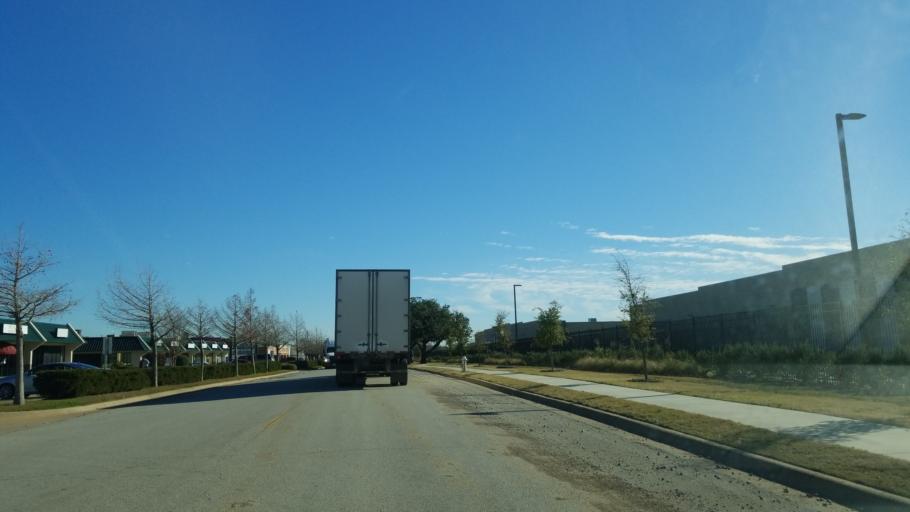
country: US
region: Texas
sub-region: Tarrant County
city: Arlington
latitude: 32.7464
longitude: -97.0595
